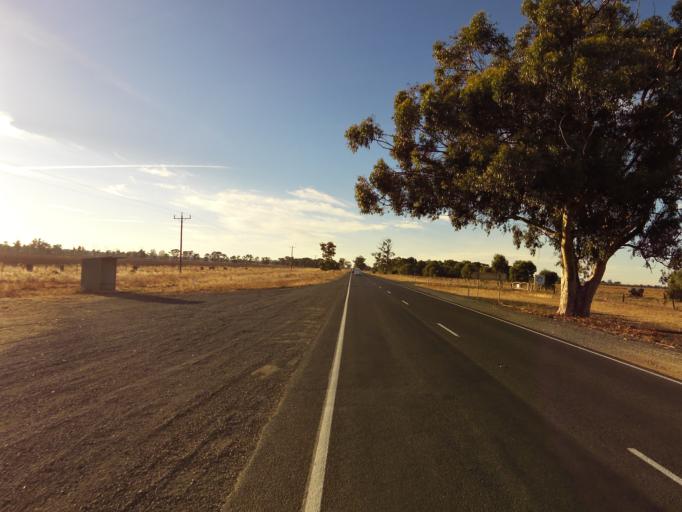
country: AU
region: New South Wales
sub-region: Murray Shire
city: Moama
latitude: -36.0976
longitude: 144.6794
